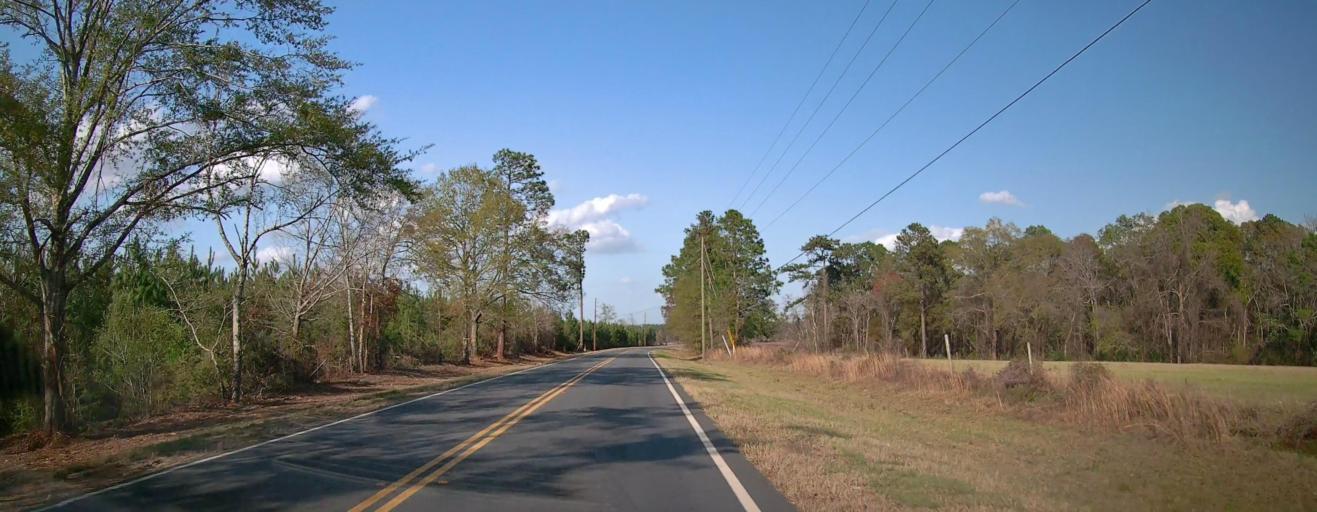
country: US
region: Georgia
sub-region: Telfair County
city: McRae
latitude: 32.0375
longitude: -82.8368
